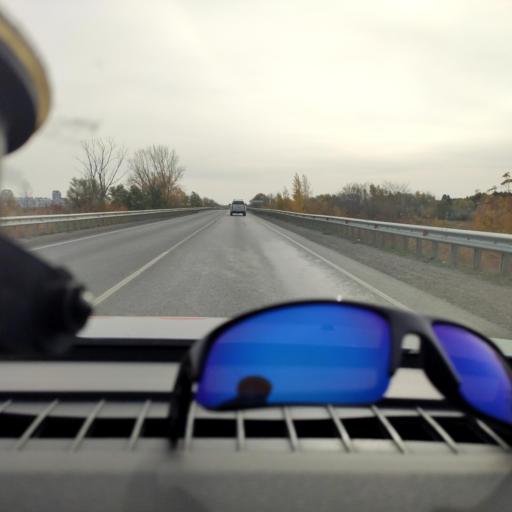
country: RU
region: Samara
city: Samara
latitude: 53.1030
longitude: 50.1388
